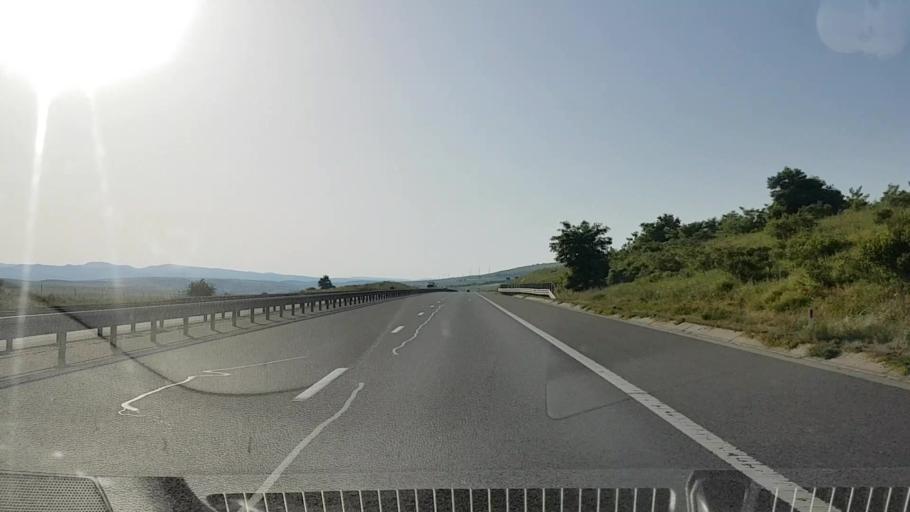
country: RO
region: Cluj
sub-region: Comuna Ciurila
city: Ciurila
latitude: 46.6128
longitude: 23.5967
